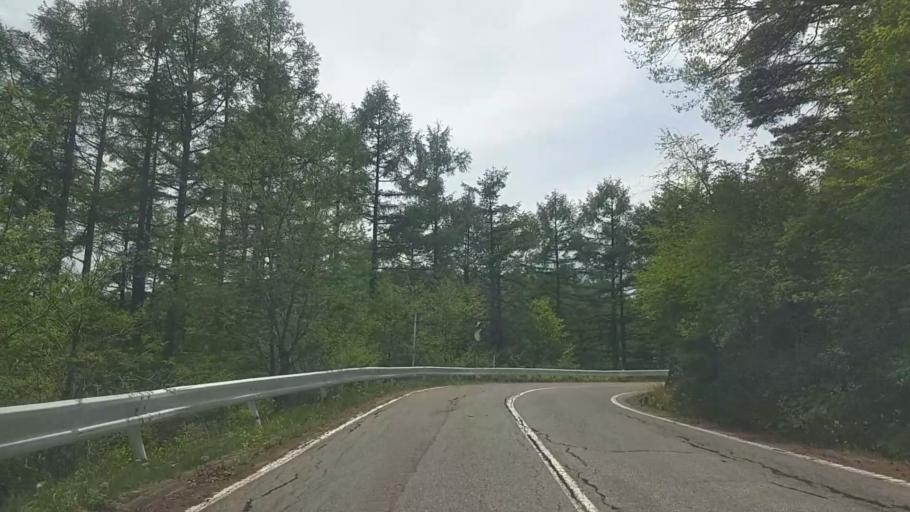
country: JP
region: Nagano
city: Saku
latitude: 36.0881
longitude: 138.3884
